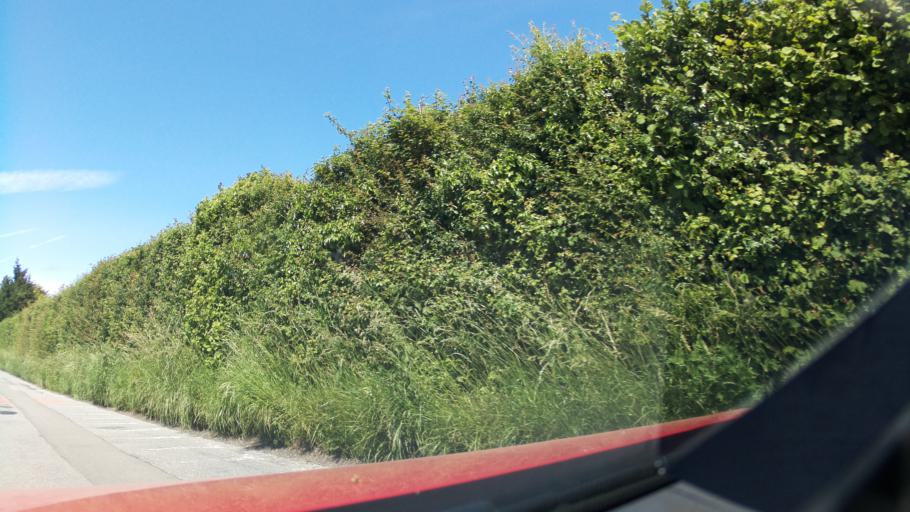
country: GB
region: Wales
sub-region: Monmouthshire
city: Caldicot
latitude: 51.5939
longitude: -2.7303
